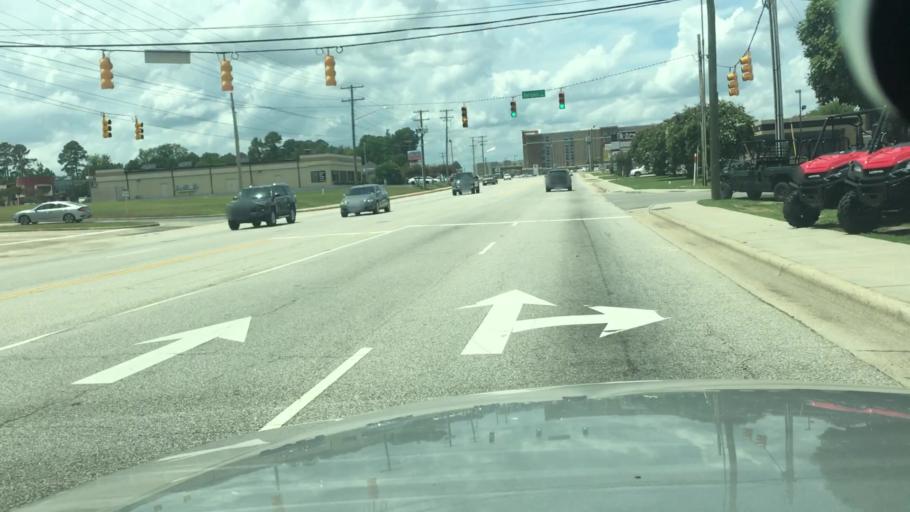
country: US
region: North Carolina
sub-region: Cumberland County
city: Fayetteville
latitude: 35.0789
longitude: -78.9432
